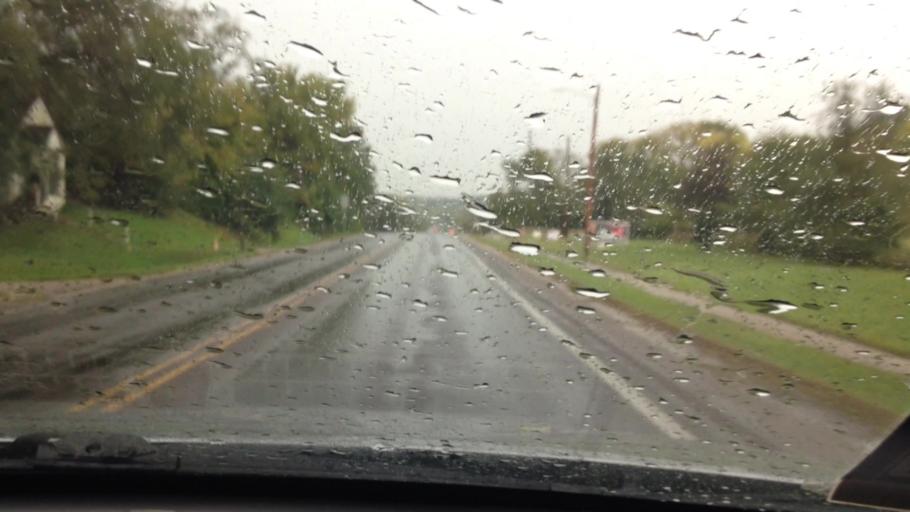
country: US
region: Kansas
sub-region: Leavenworth County
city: Leavenworth
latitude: 39.3103
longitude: -94.9401
